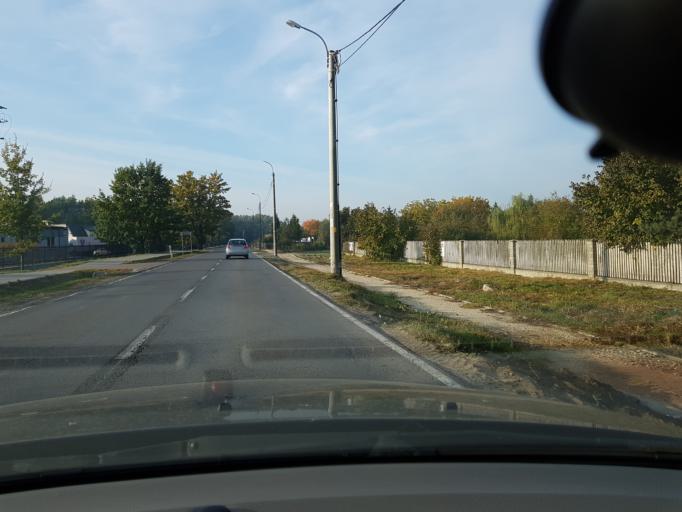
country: PL
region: Masovian Voivodeship
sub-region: Powiat otwocki
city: Jozefow
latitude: 52.1795
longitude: 21.2981
